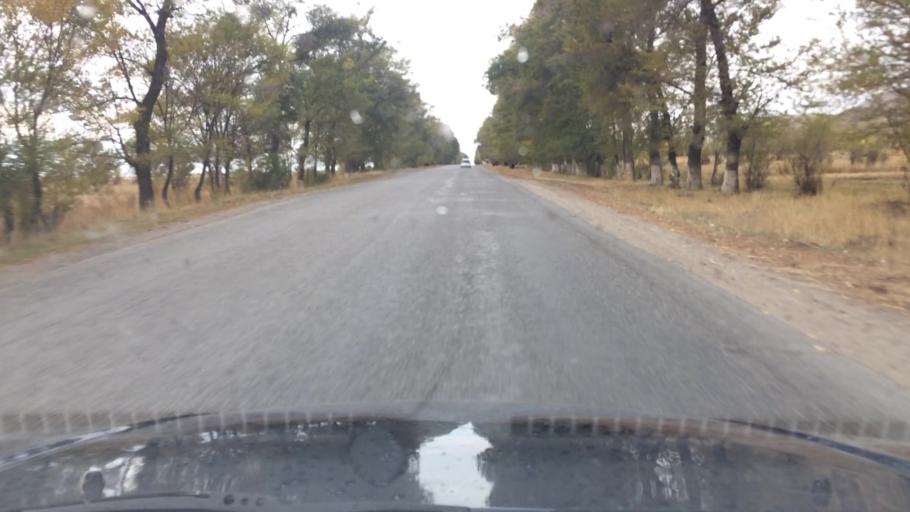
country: KG
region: Ysyk-Koel
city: Tyup
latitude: 42.7374
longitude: 77.9950
